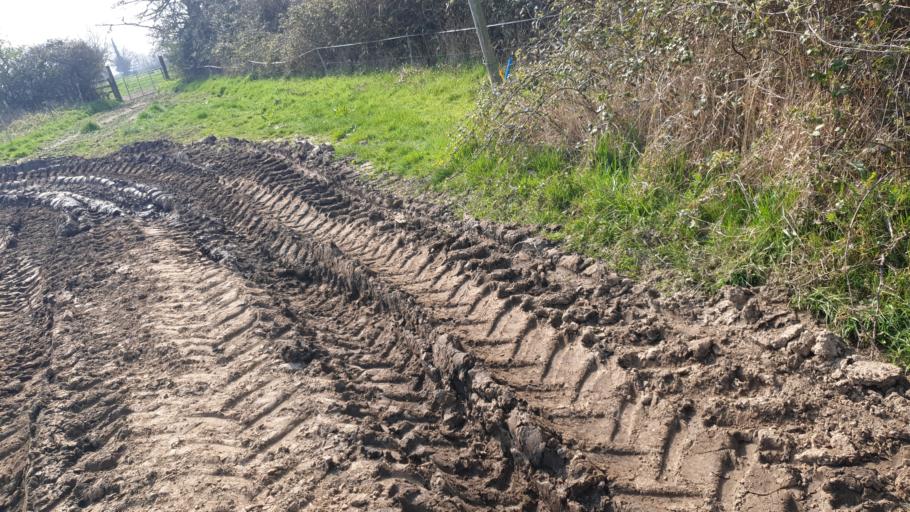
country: GB
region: England
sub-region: Essex
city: Mistley
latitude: 51.9236
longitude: 1.1583
